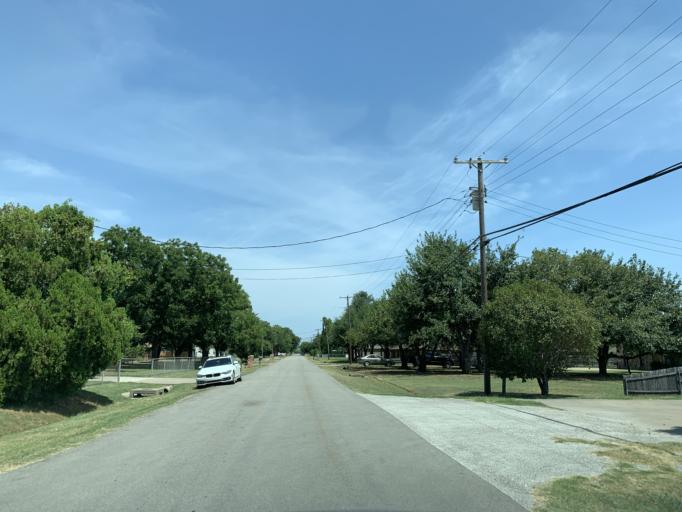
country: US
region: Texas
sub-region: Dallas County
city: Cedar Hill
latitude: 32.6475
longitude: -97.0206
